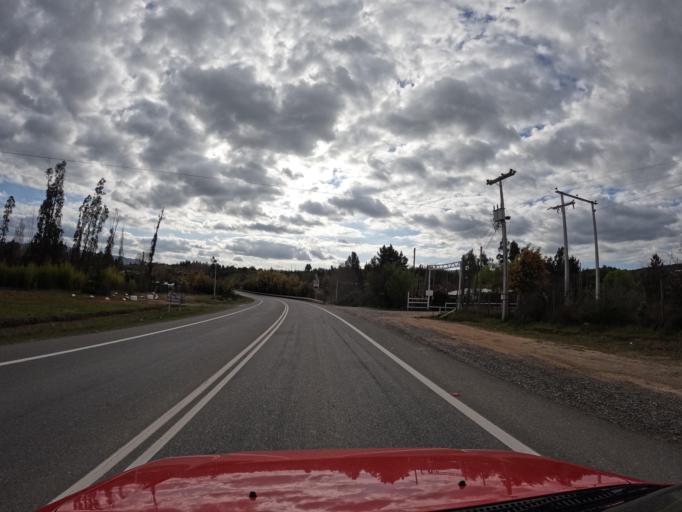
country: CL
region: Maule
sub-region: Provincia de Linares
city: San Javier
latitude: -35.5587
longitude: -72.0821
